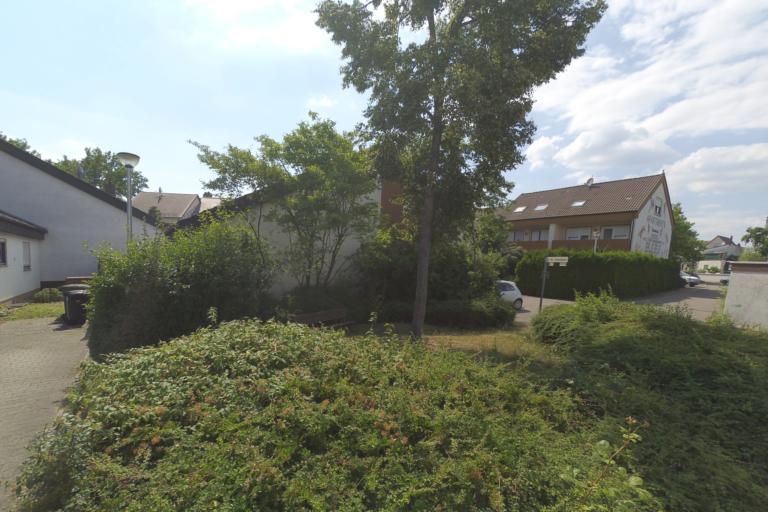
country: DE
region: Hesse
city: Viernheim
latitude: 49.5305
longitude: 8.5779
